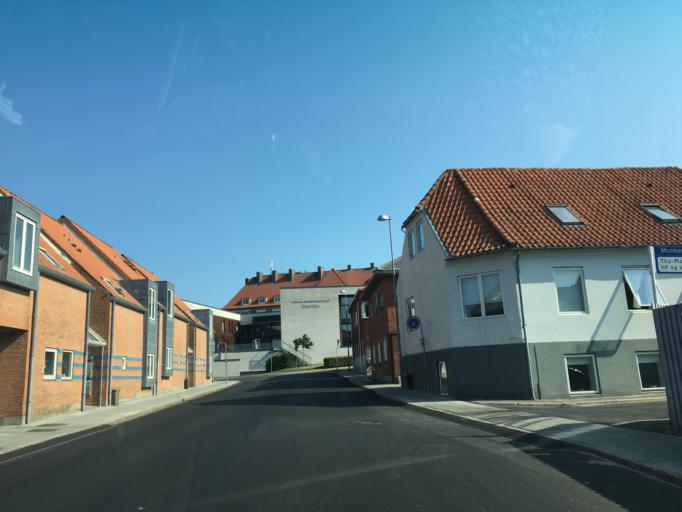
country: DK
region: North Denmark
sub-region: Thisted Kommune
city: Thisted
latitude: 56.9559
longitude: 8.6955
